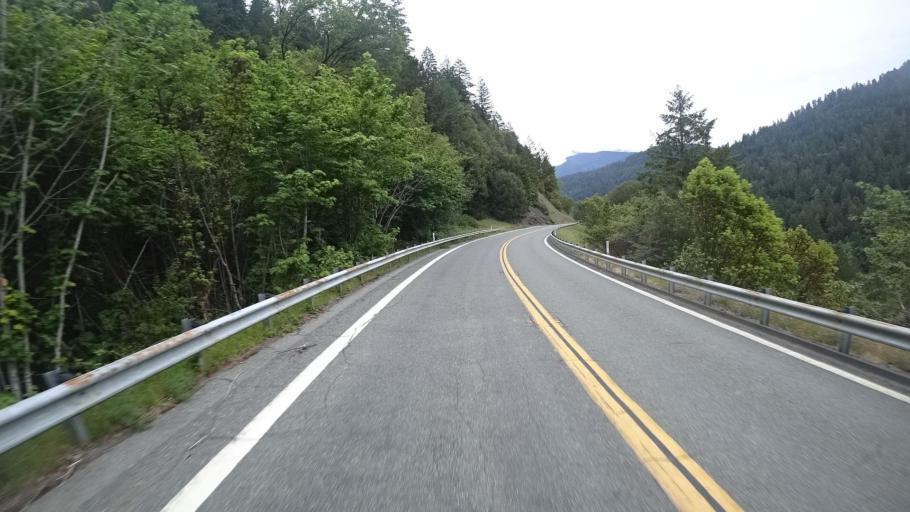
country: US
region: California
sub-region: Humboldt County
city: Willow Creek
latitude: 41.2777
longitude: -123.5938
